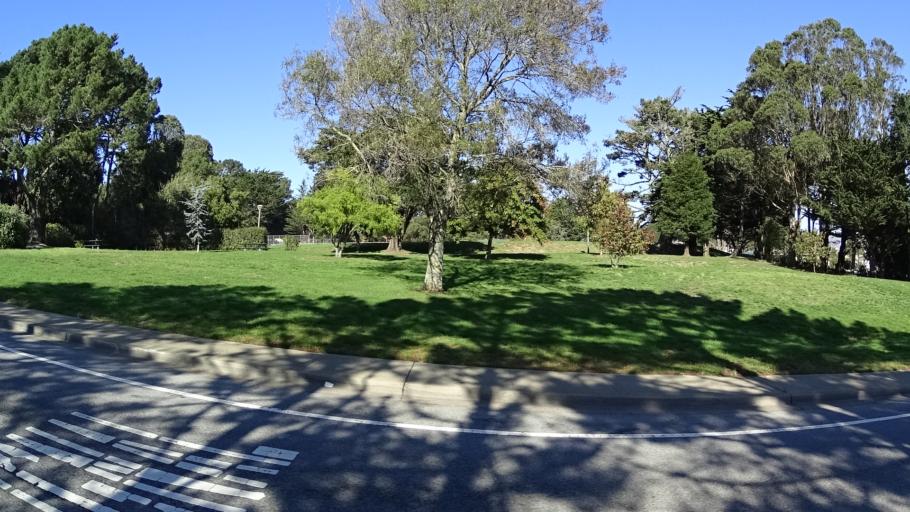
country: US
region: California
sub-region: San Mateo County
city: Colma
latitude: 37.6434
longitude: -122.4581
